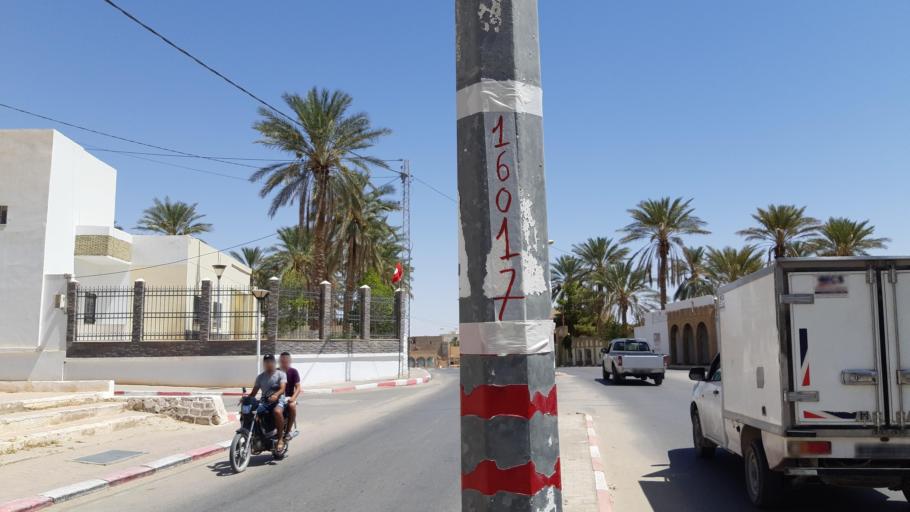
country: TN
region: Tawzar
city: Degache
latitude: 33.9849
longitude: 8.2173
